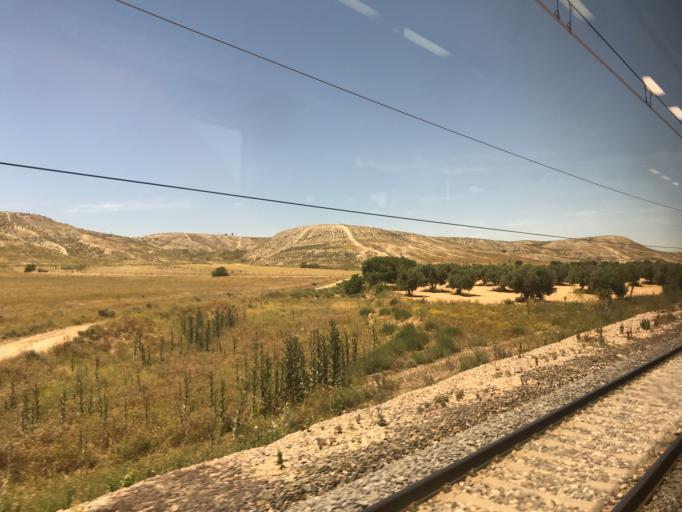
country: ES
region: Madrid
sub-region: Provincia de Madrid
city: Ciempozuelos
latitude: 40.1229
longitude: -3.6180
